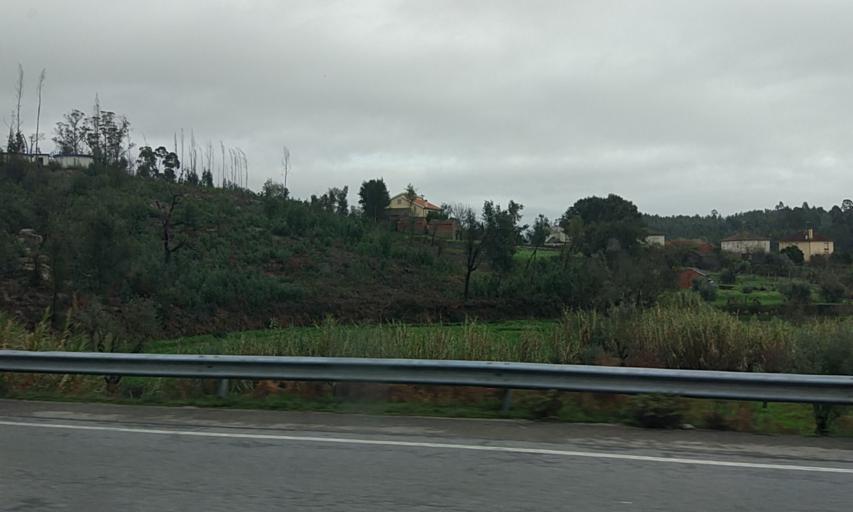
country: PT
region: Viseu
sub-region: Santa Comba Dao
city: Santa Comba Dao
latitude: 40.4219
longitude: -8.1197
